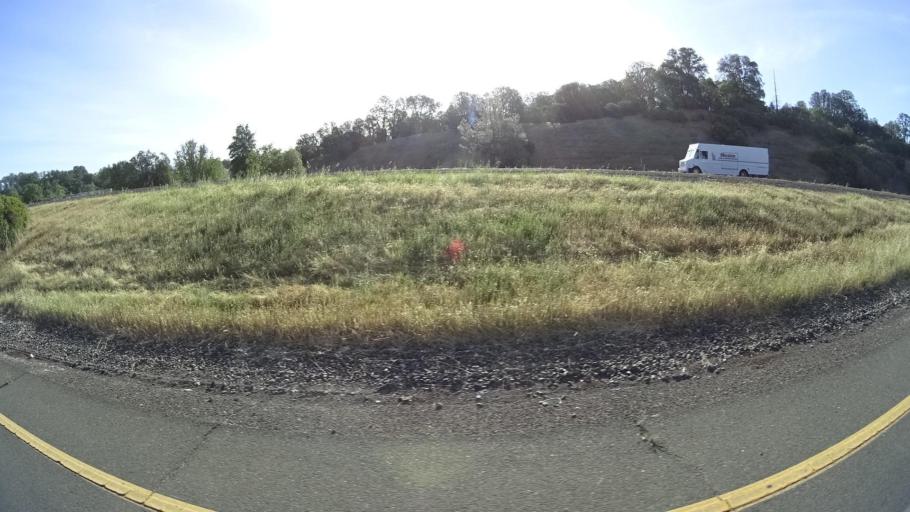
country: US
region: California
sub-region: Lake County
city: Lakeport
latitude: 39.0492
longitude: -122.9319
